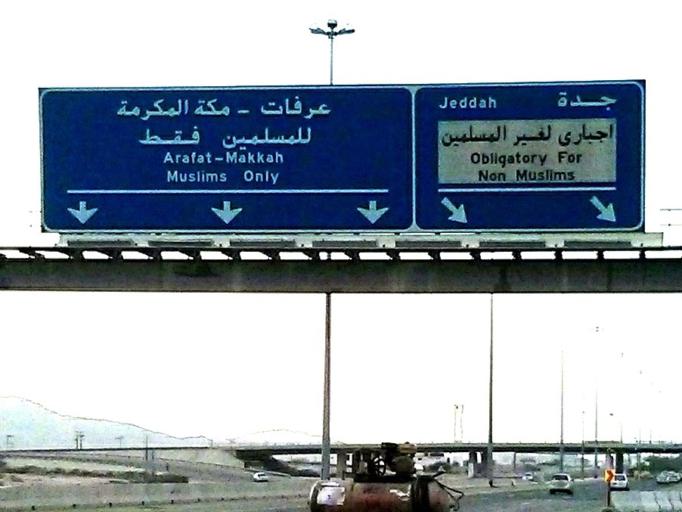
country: SA
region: Makkah
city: Al Hada
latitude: 21.3450
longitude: 40.2557
